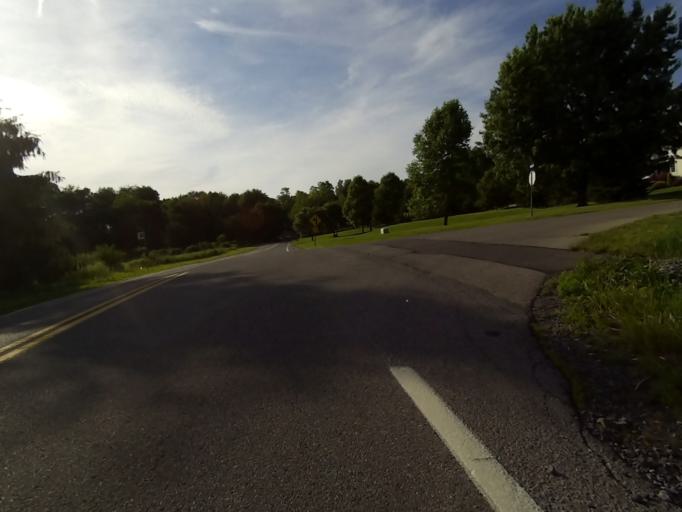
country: US
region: Pennsylvania
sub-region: Centre County
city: Park Forest Village
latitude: 40.8146
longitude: -77.9581
